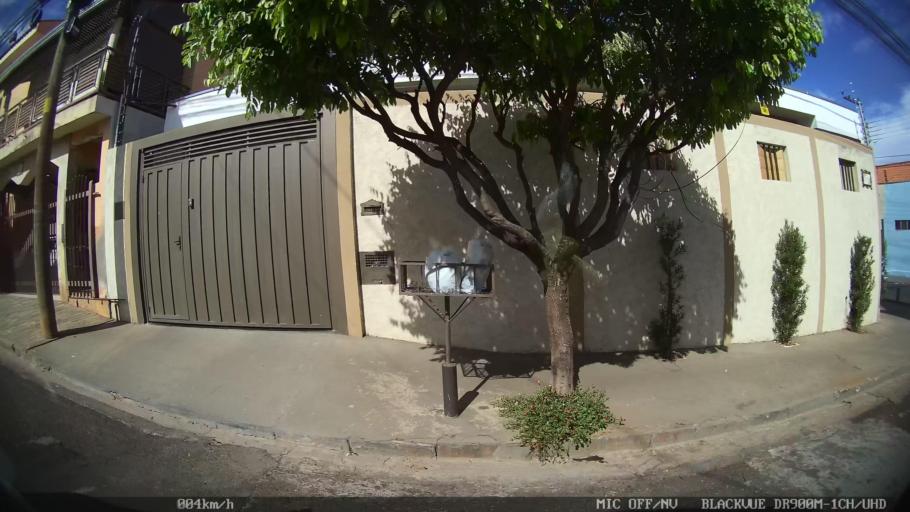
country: BR
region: Sao Paulo
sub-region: Catanduva
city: Catanduva
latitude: -21.1260
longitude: -48.9742
